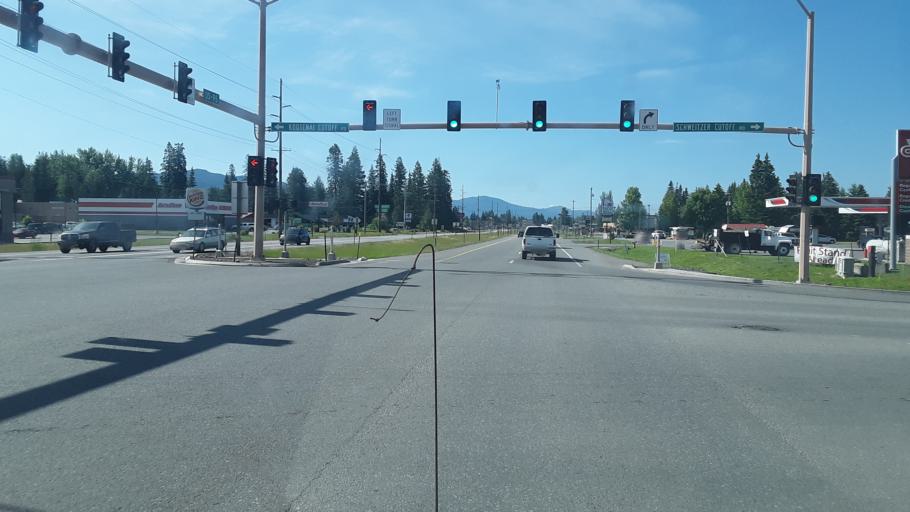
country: US
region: Idaho
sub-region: Bonner County
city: Ponderay
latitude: 48.3093
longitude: -116.5464
